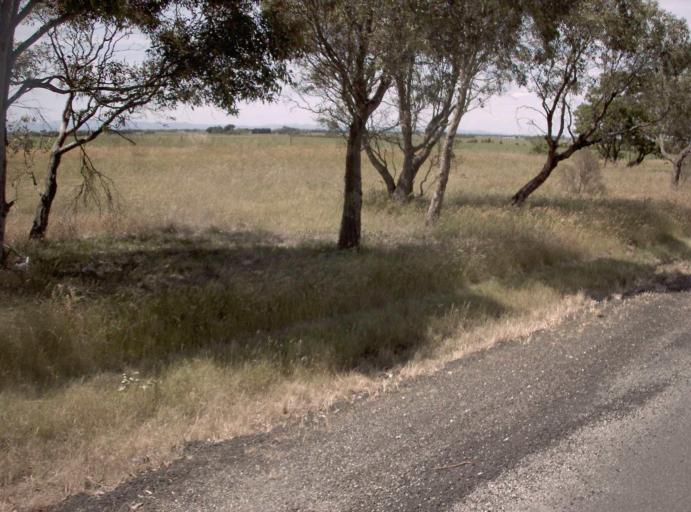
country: AU
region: Victoria
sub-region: Wellington
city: Heyfield
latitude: -38.1158
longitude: 146.8712
